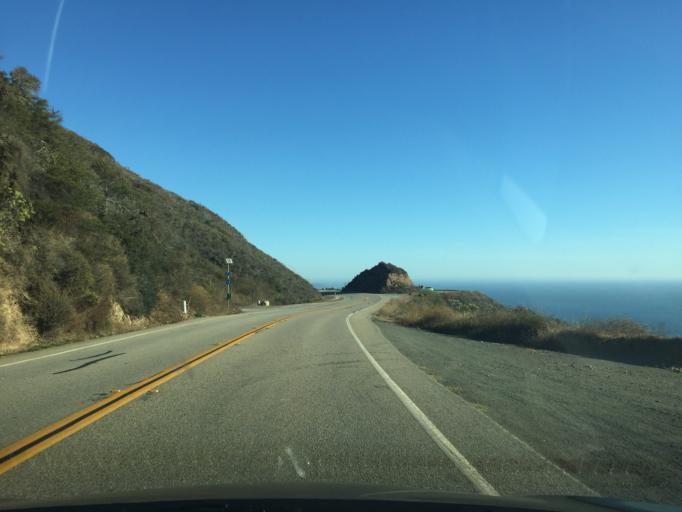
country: US
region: California
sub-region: San Luis Obispo County
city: Cambria
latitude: 35.8278
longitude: -121.3867
